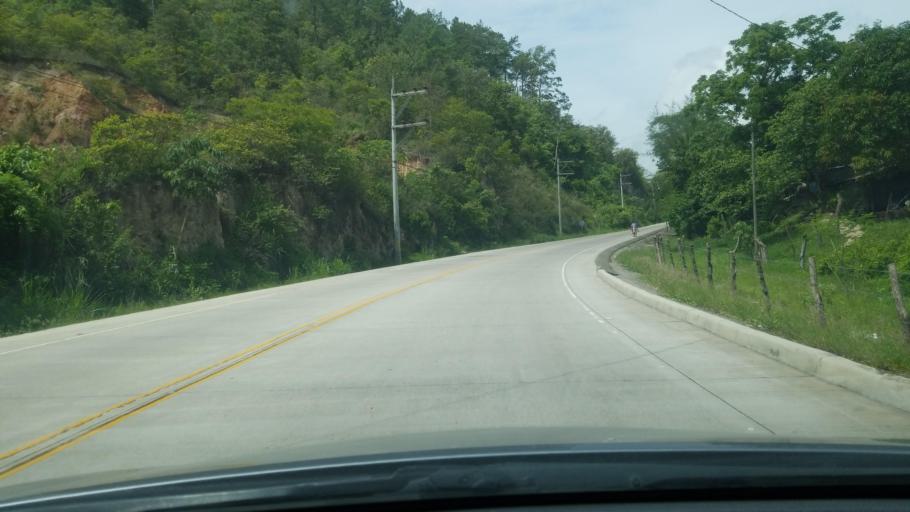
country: HN
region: Copan
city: La Entrada
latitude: 15.0401
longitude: -88.7645
